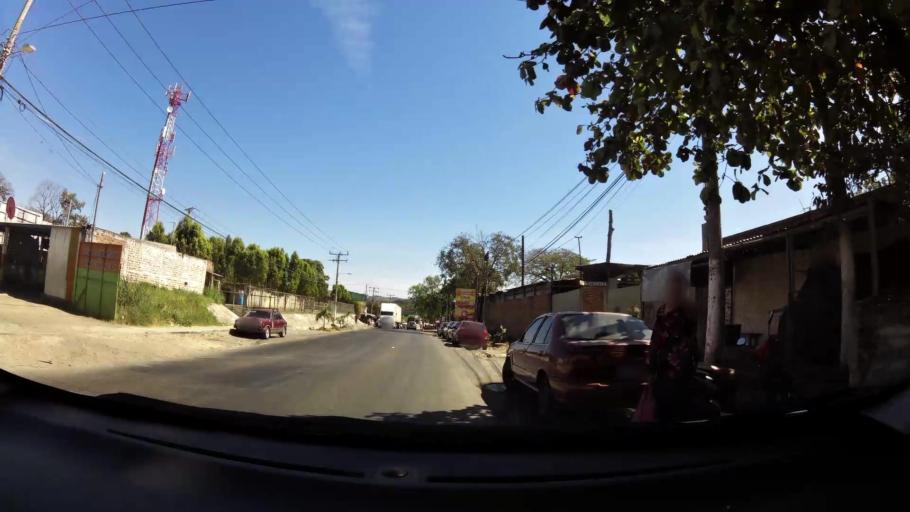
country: SV
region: San Salvador
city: Apopa
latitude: 13.7957
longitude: -89.1792
